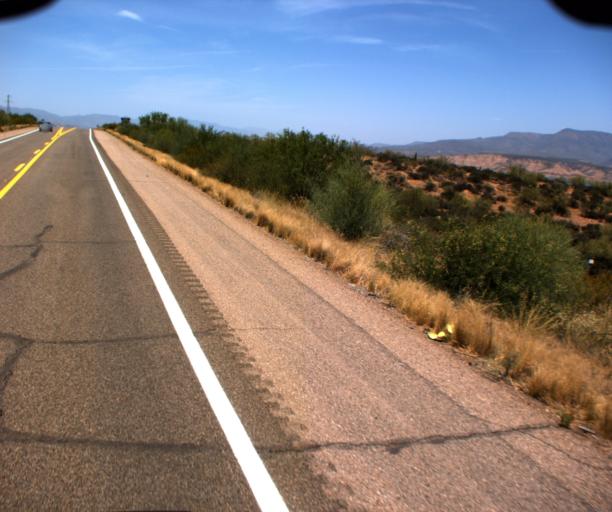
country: US
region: Arizona
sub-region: Gila County
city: Tonto Basin
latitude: 33.6527
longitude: -111.1028
